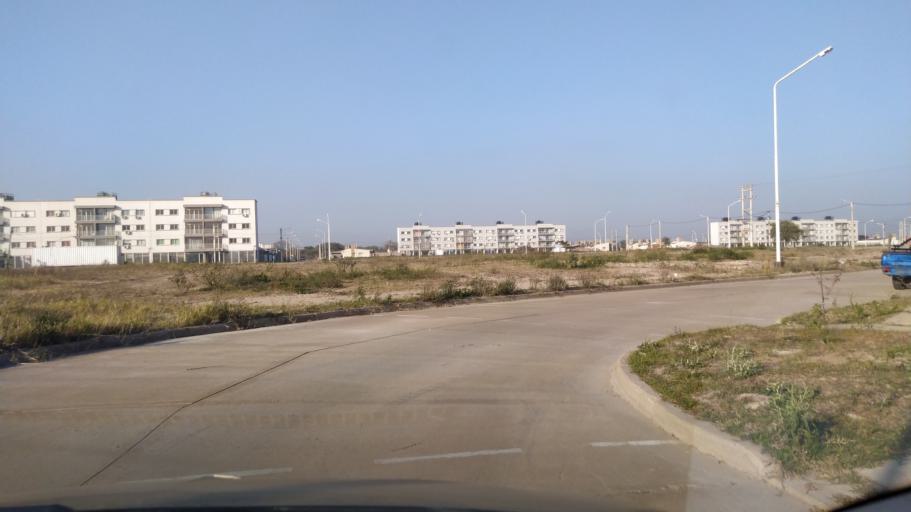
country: AR
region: Corrientes
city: Corrientes
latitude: -27.5251
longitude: -58.8045
